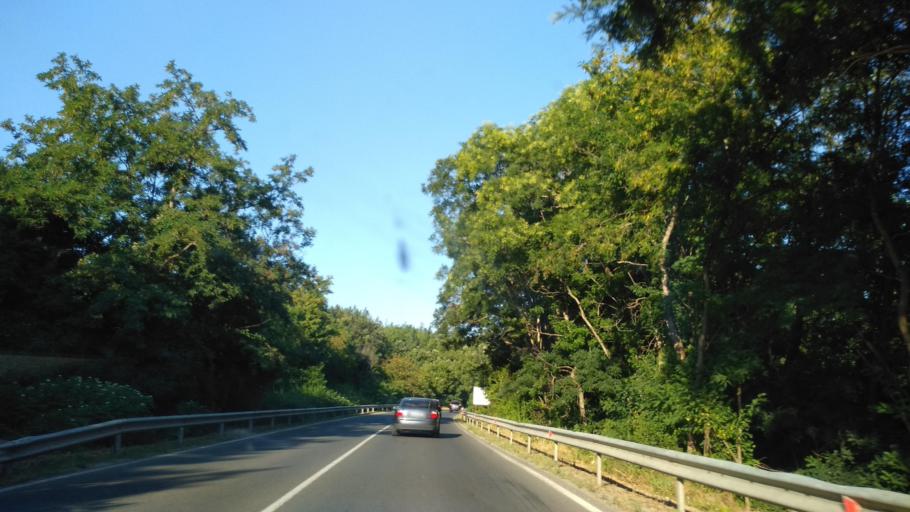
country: BG
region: Veliko Turnovo
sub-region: Obshtina Pavlikeni
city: Byala Cherkva
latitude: 43.0681
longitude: 25.3055
